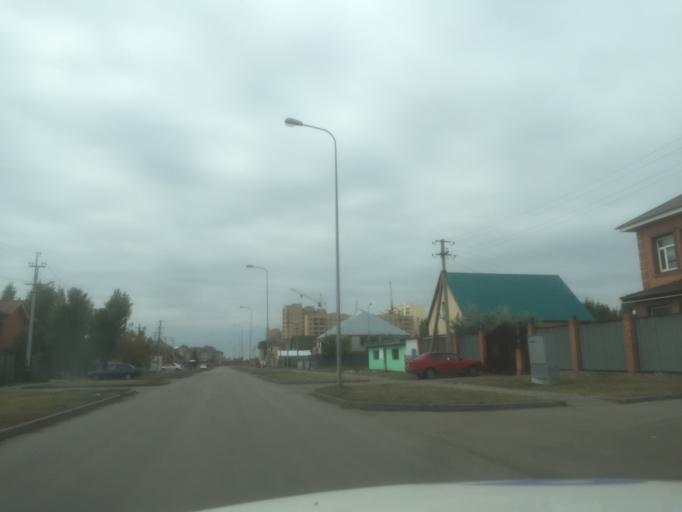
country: KZ
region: Astana Qalasy
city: Astana
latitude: 51.1759
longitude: 71.3738
